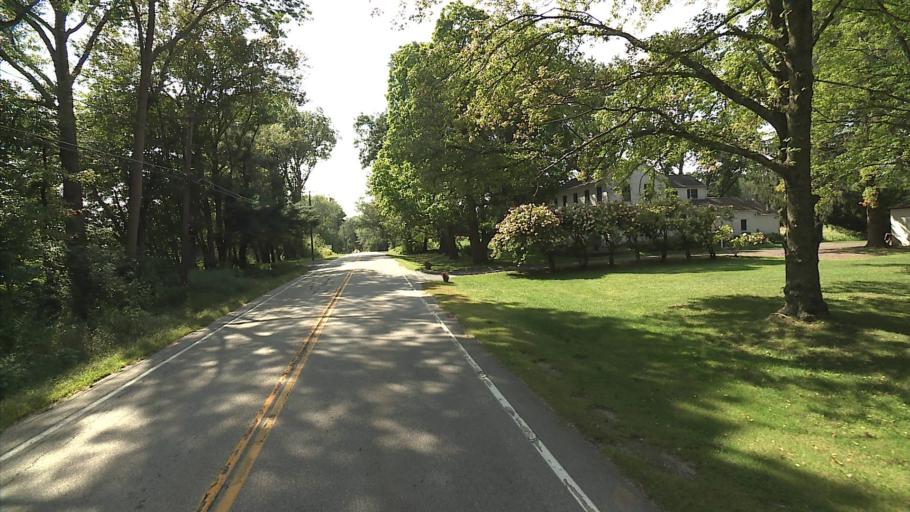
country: US
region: Connecticut
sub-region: Windham County
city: South Woodstock
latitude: 41.9242
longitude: -71.9568
